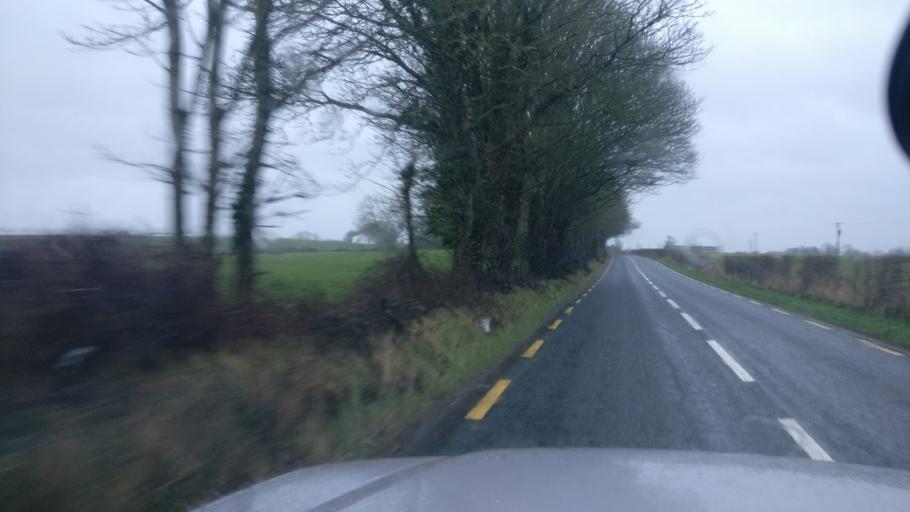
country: IE
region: Connaught
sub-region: County Galway
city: Ballinasloe
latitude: 53.2579
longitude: -8.1832
